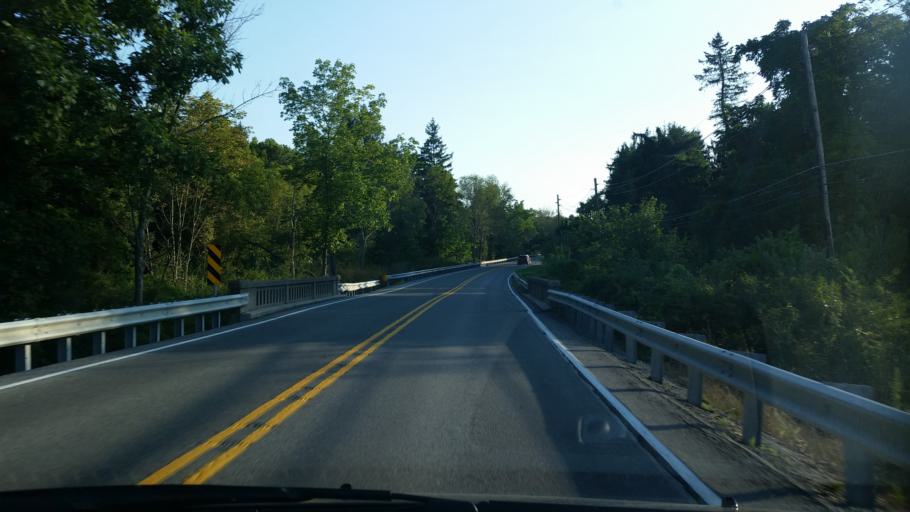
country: US
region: Pennsylvania
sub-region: Blair County
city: Greenwood
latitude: 40.5748
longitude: -78.3709
